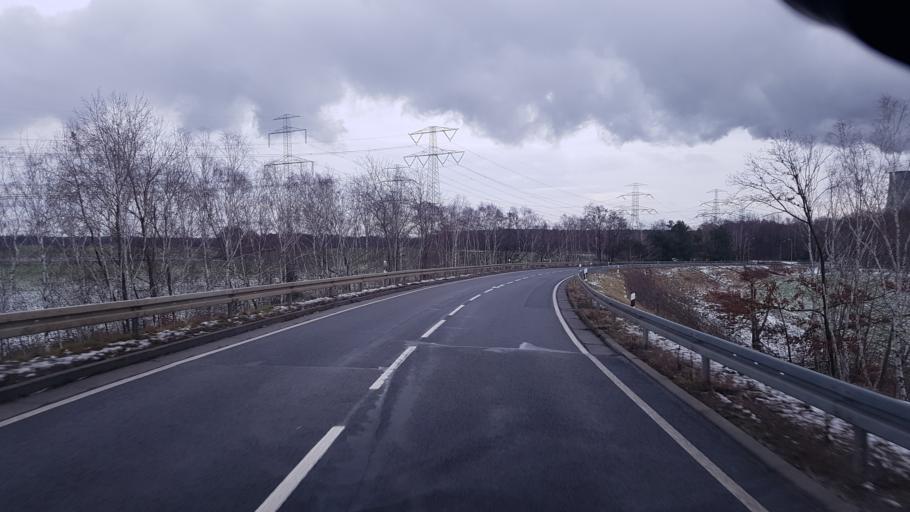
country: DE
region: Brandenburg
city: Peitz
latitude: 51.8481
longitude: 14.4545
